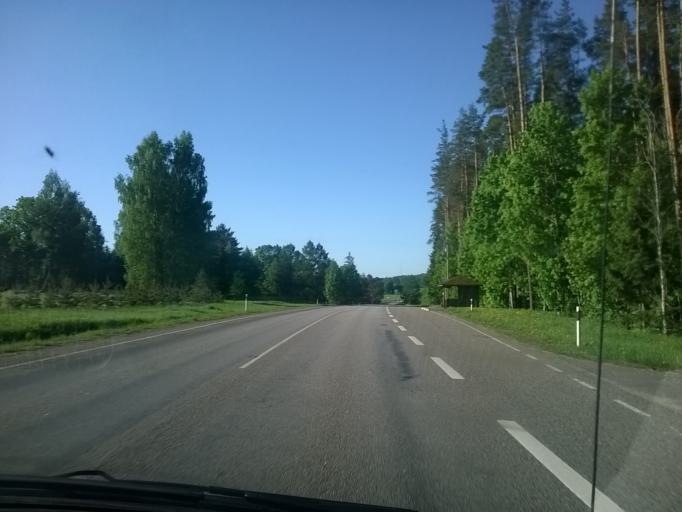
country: EE
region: Valgamaa
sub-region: Torva linn
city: Torva
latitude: 57.9873
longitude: 26.1737
